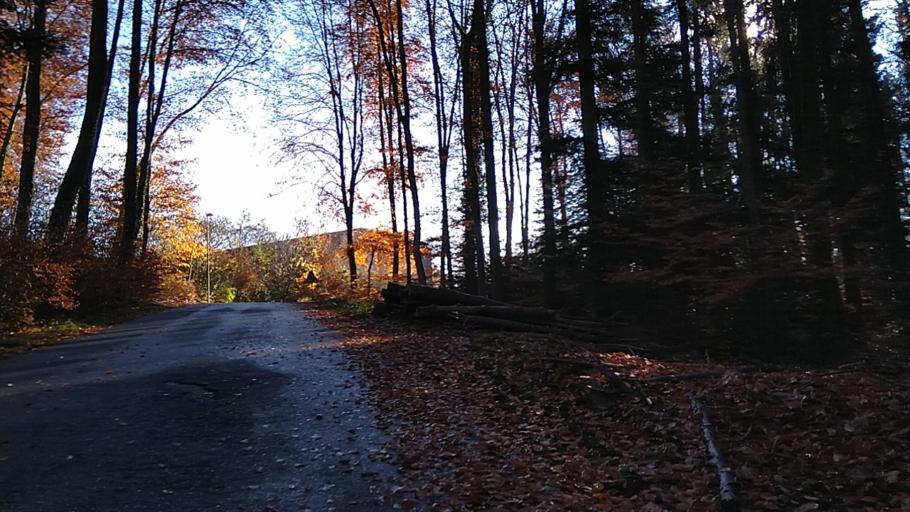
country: CH
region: Bern
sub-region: Bern-Mittelland District
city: Kirchlindach
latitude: 46.9733
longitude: 7.4111
